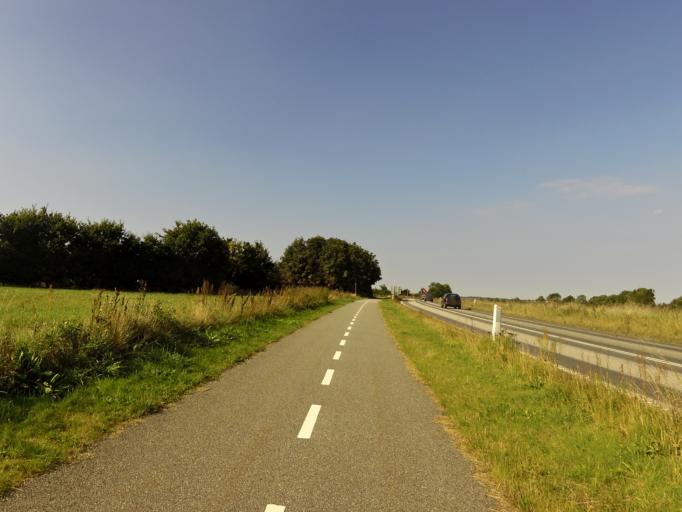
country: DK
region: South Denmark
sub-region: Vejen Kommune
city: Vejen
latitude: 55.4255
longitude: 9.1487
